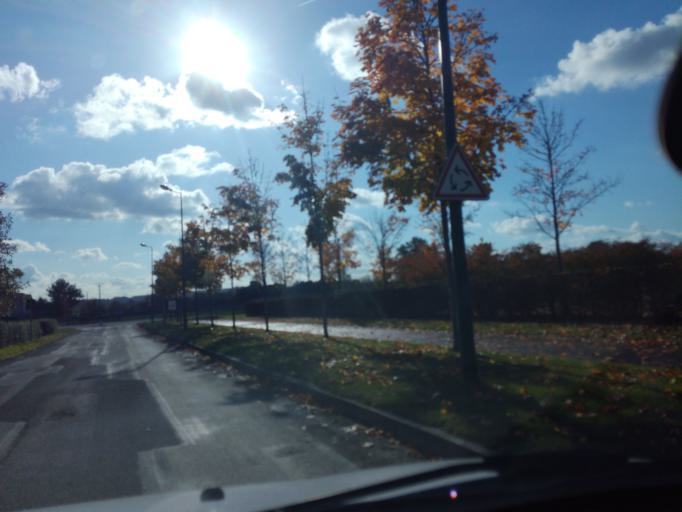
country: FR
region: Brittany
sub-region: Departement d'Ille-et-Vilaine
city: Chavagne
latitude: 48.0543
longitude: -1.8004
